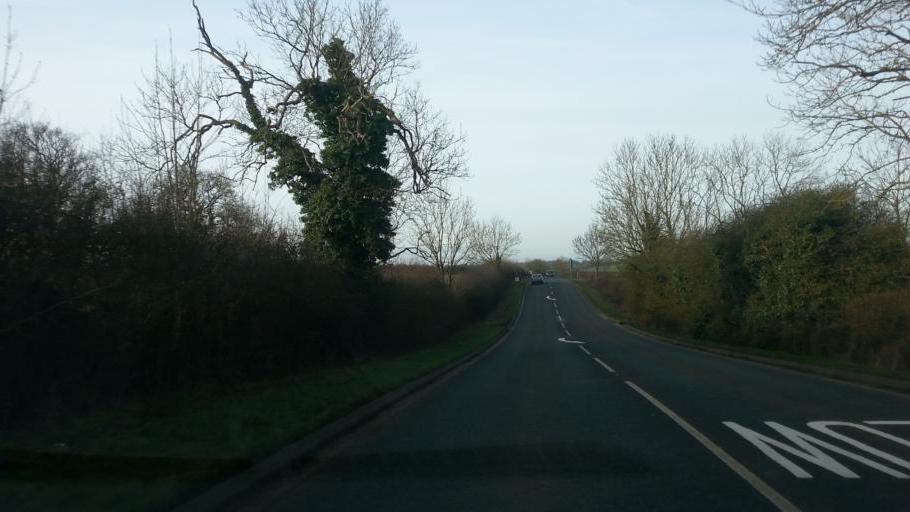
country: GB
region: England
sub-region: Leicestershire
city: Wymondham
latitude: 52.8513
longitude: -0.7676
